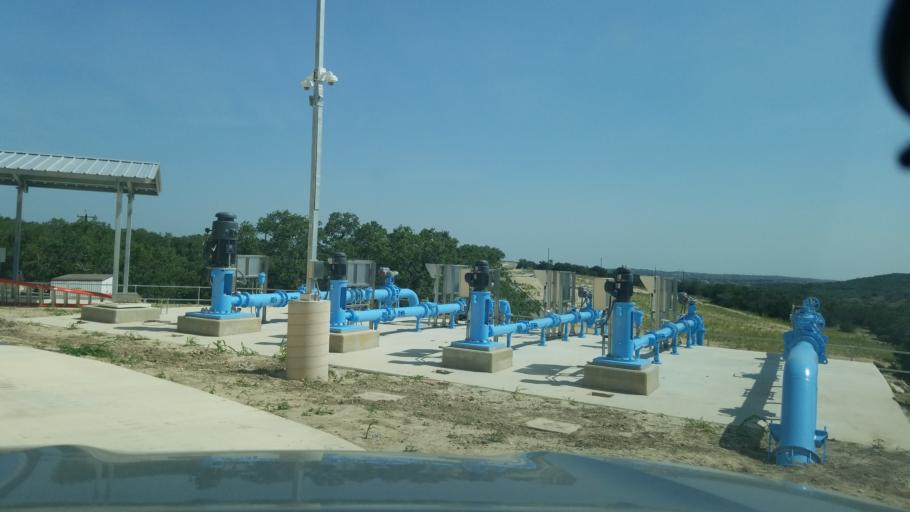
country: US
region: Texas
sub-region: Bexar County
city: Timberwood Park
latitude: 29.7066
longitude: -98.4673
